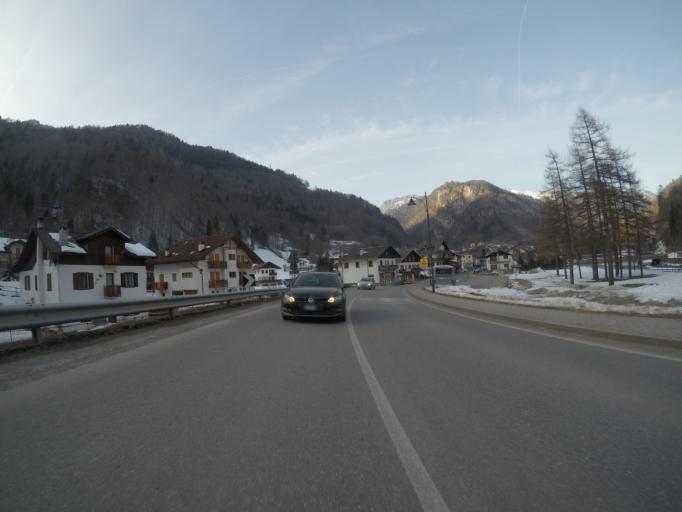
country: IT
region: Veneto
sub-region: Provincia di Belluno
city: Cencenighe Agordino
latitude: 46.3463
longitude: 11.9699
